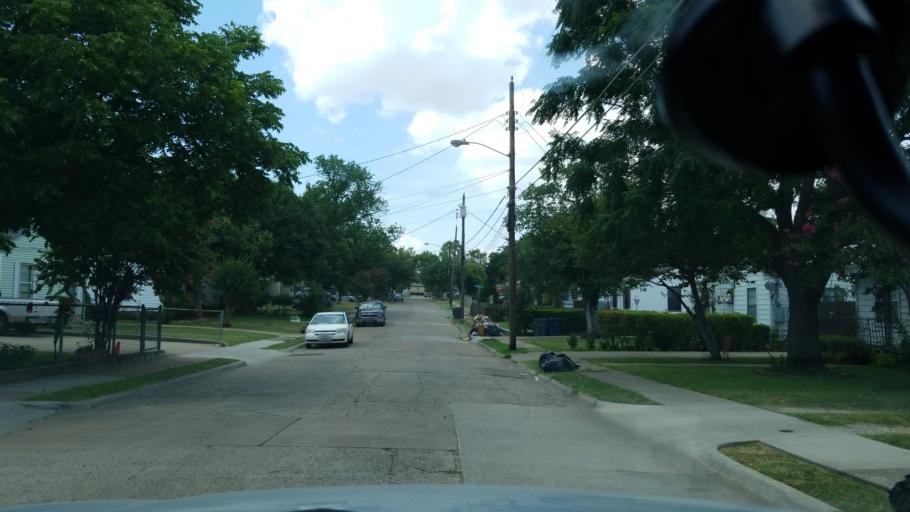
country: US
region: Texas
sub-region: Dallas County
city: Cockrell Hill
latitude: 32.7324
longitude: -96.8804
